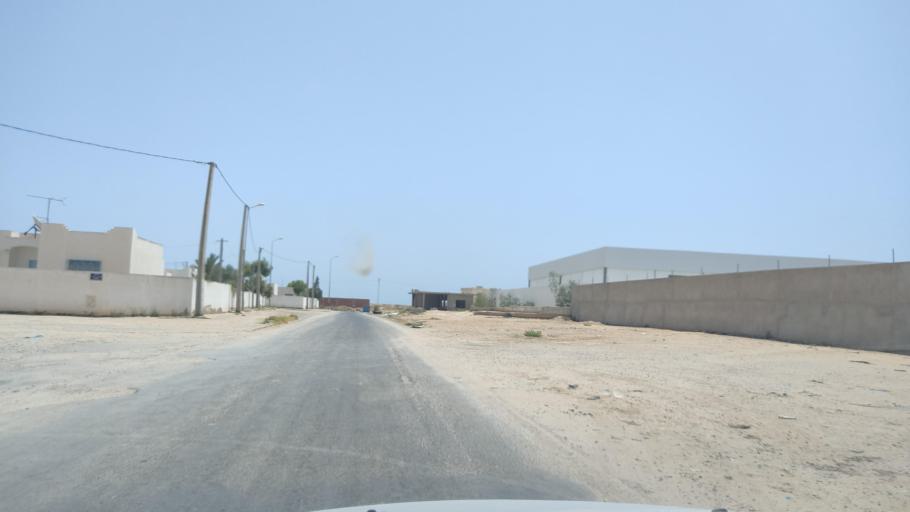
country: TN
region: Safaqis
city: Sfax
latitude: 34.6625
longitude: 10.7019
